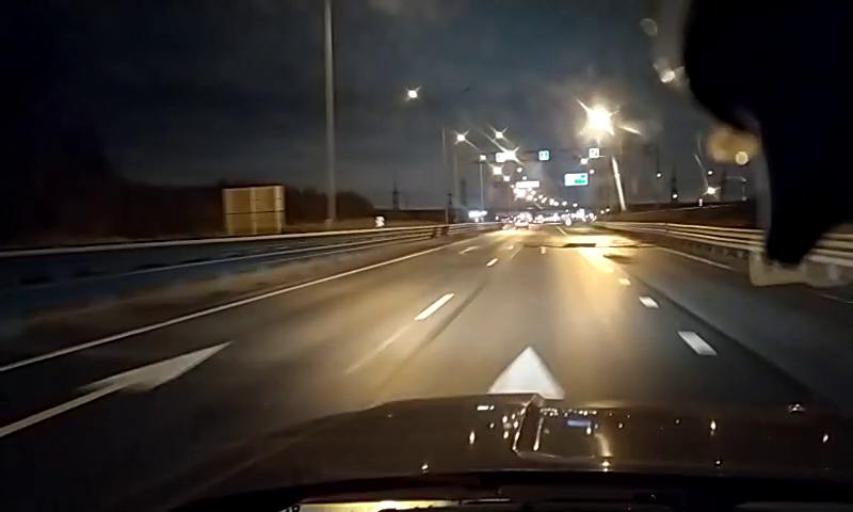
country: RU
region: Leningrad
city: Bugry
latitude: 60.1038
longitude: 30.3854
